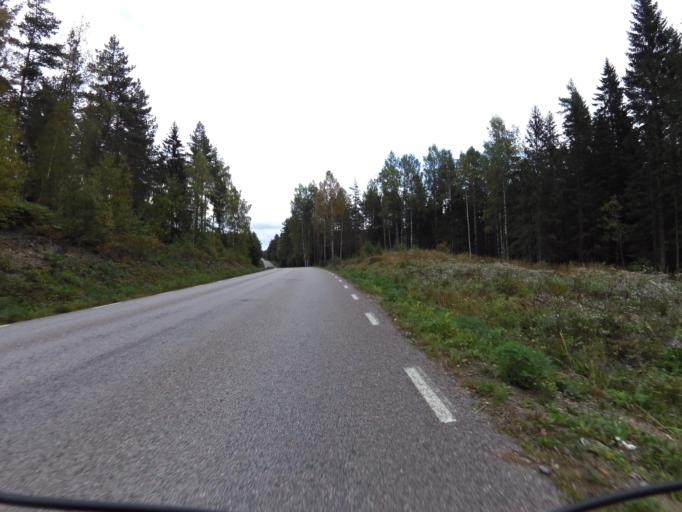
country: SE
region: Gaevleborg
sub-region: Sandvikens Kommun
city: Sandviken
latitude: 60.6514
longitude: 16.8293
